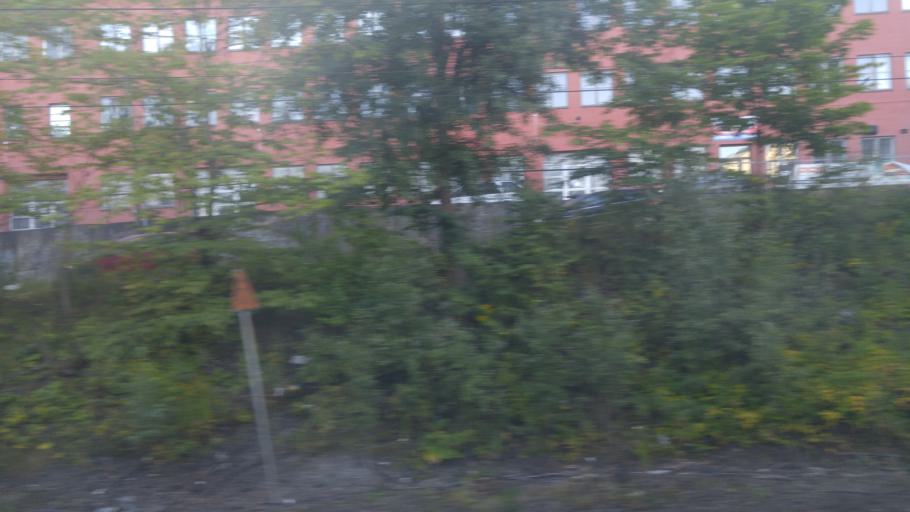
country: NO
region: Oslo
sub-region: Oslo
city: Oslo
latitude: 59.9113
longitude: 10.8254
